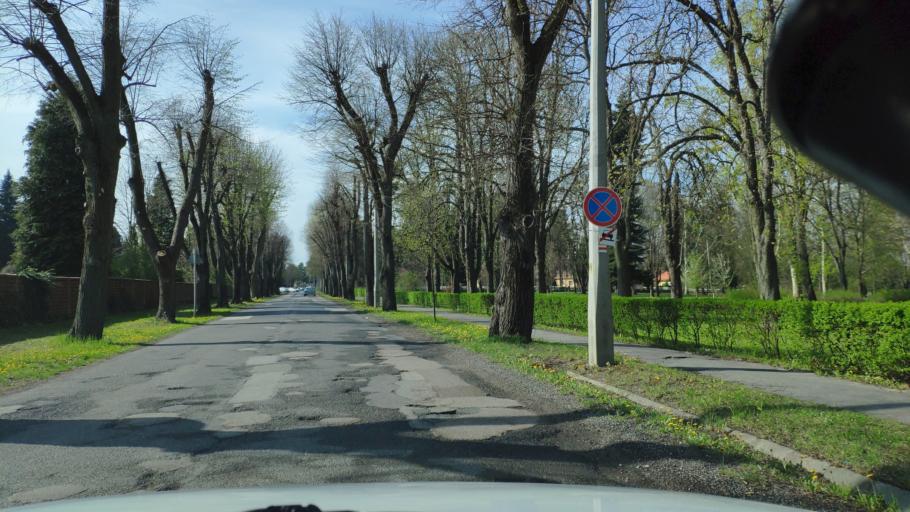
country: HU
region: Zala
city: Nagykanizsa
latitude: 46.4498
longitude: 16.9967
